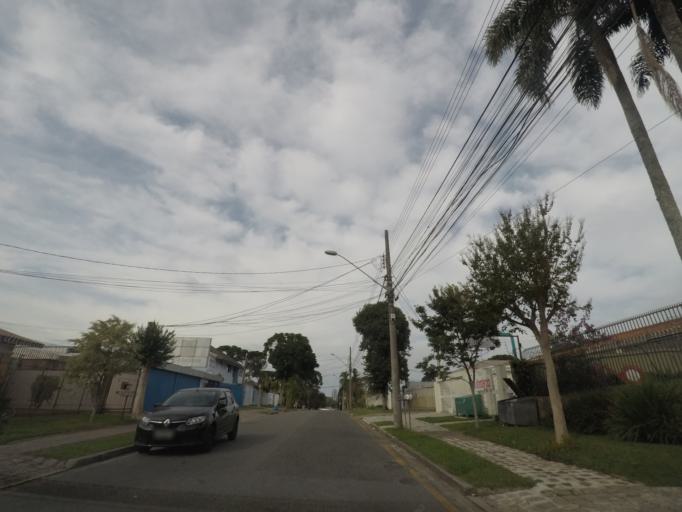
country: BR
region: Parana
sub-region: Curitiba
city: Curitiba
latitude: -25.4088
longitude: -49.2741
